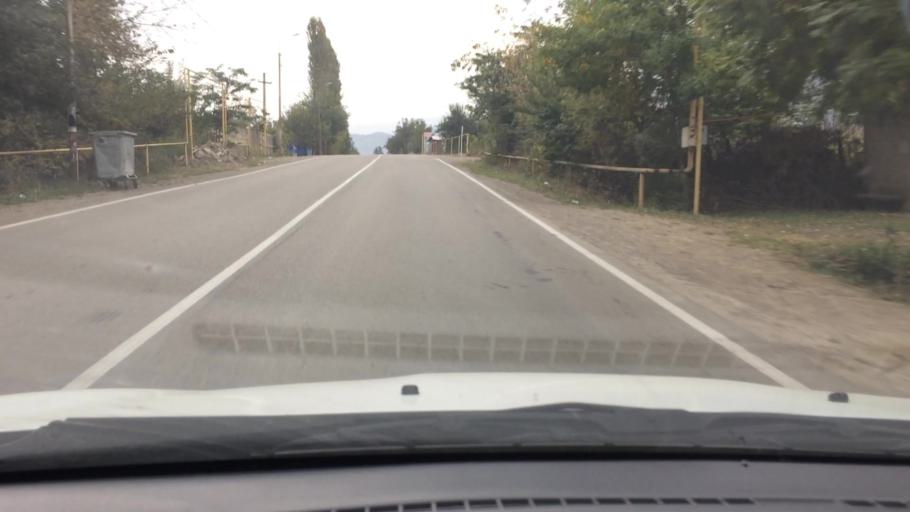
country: AM
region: Tavush
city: Bagratashen
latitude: 41.2369
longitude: 44.8052
